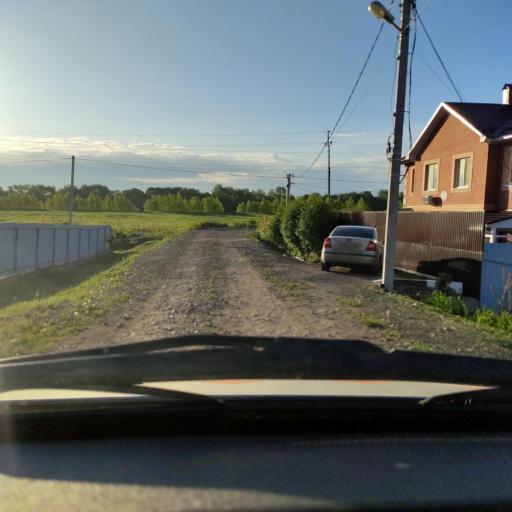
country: RU
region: Bashkortostan
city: Ufa
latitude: 54.8384
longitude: 56.0054
